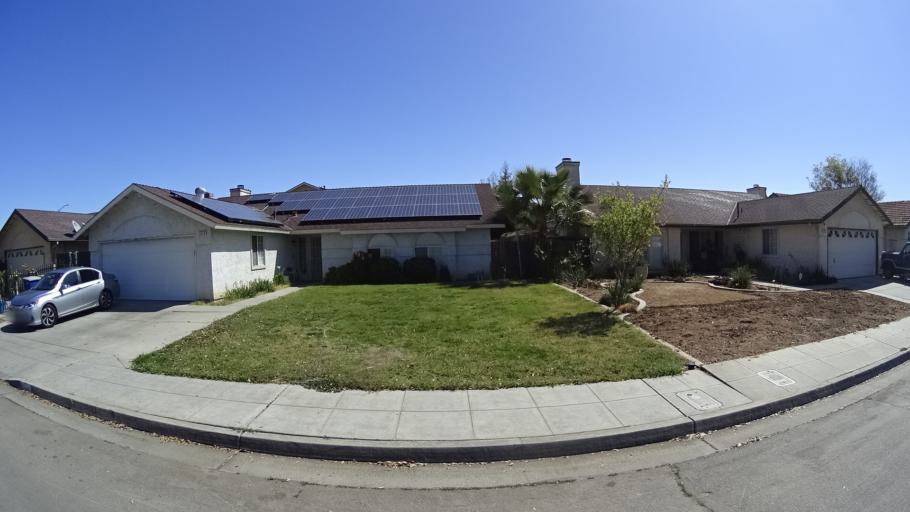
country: US
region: California
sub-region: Fresno County
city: West Park
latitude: 36.7845
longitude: -119.8831
